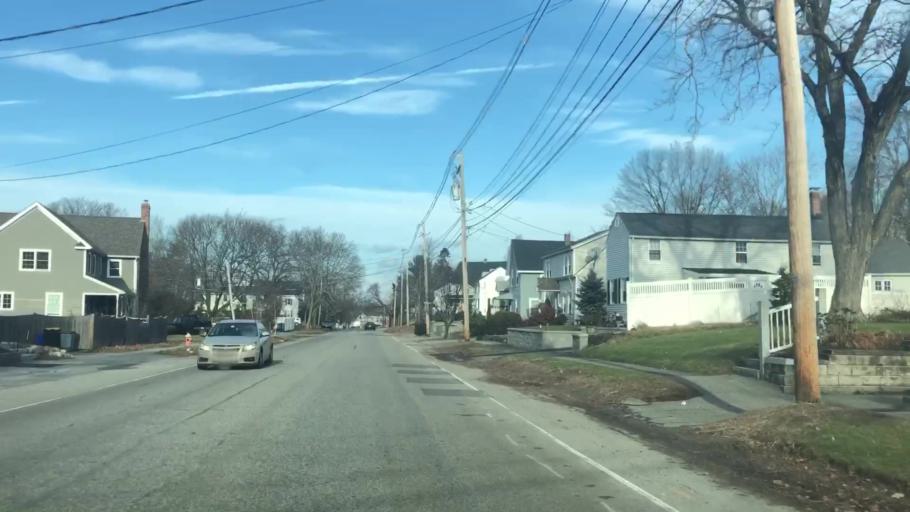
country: US
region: Massachusetts
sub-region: Essex County
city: North Andover
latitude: 42.7006
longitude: -71.1348
